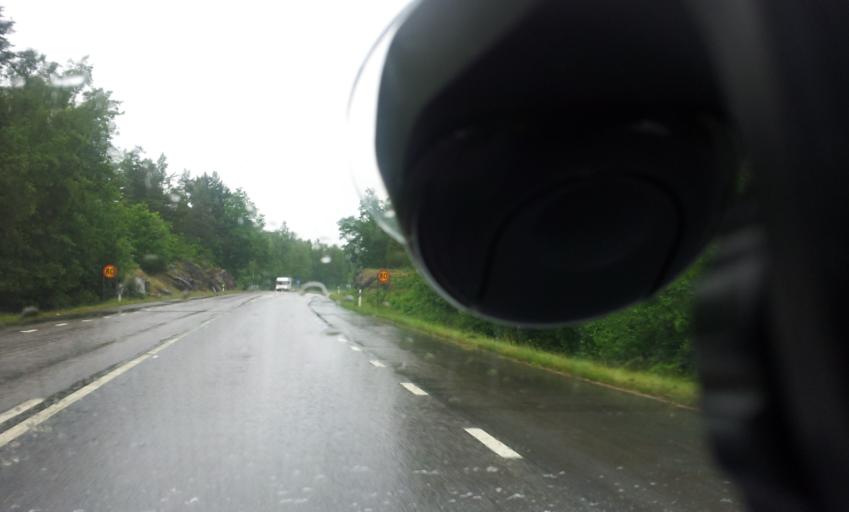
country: SE
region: Kalmar
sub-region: Vasterviks Kommun
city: Ankarsrum
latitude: 57.7199
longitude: 16.4516
